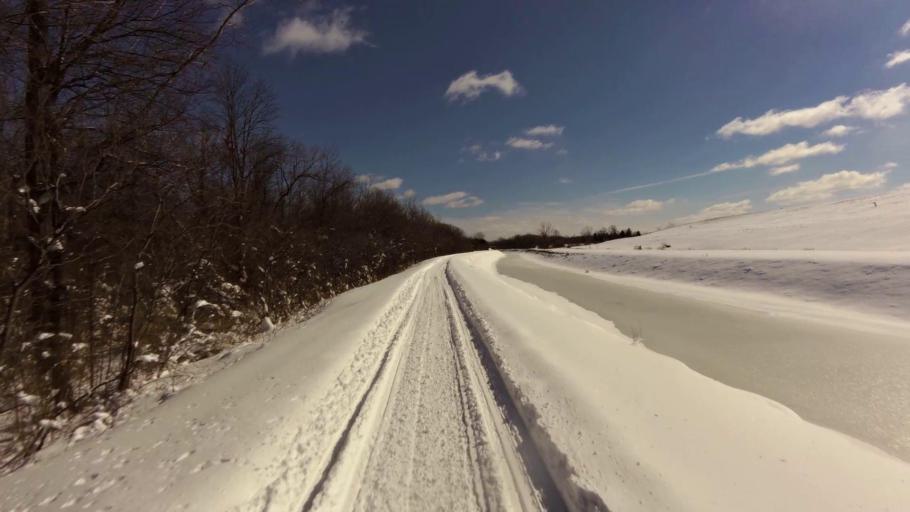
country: US
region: New York
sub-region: Orleans County
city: Albion
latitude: 43.2516
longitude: -78.1223
